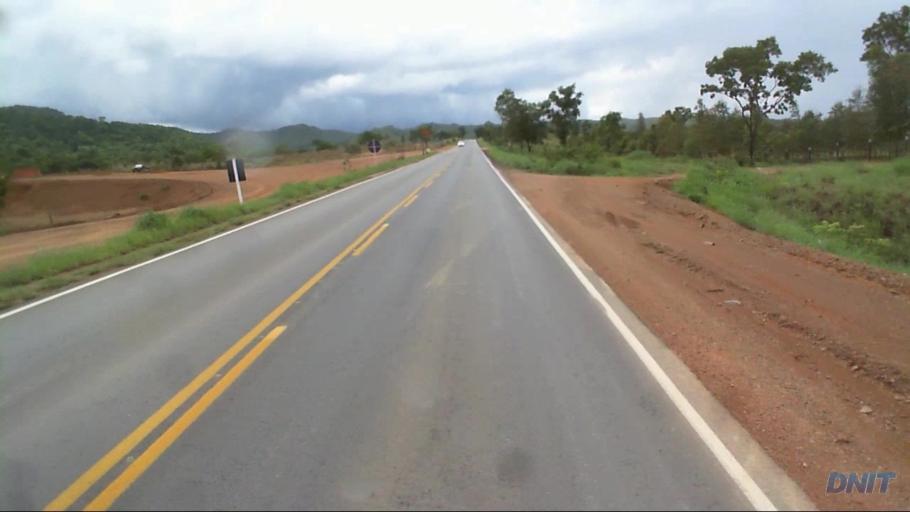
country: BR
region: Goias
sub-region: Padre Bernardo
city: Padre Bernardo
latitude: -15.4259
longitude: -48.1961
